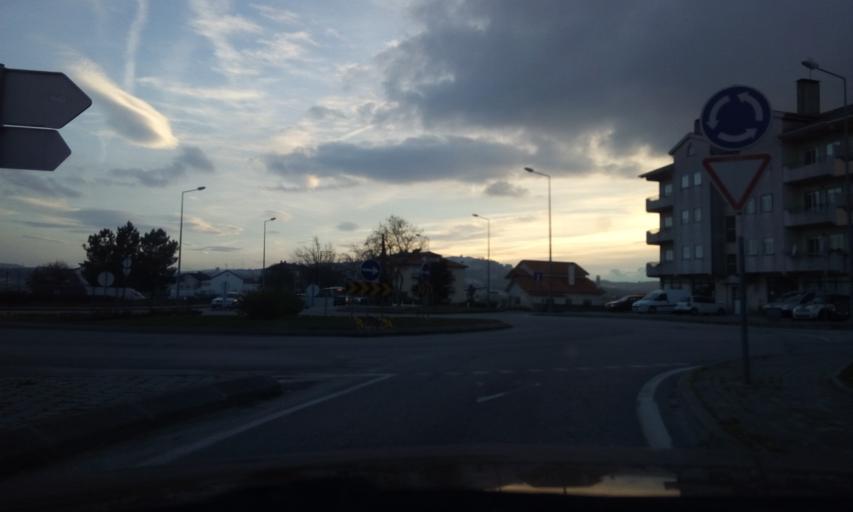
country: PT
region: Guarda
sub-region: Guarda
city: Sequeira
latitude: 40.5594
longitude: -7.2342
